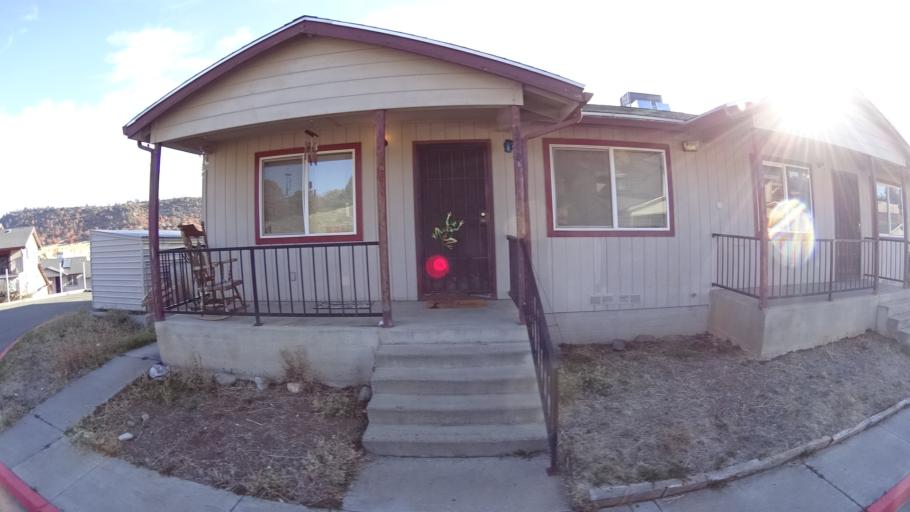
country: US
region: California
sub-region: Siskiyou County
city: Yreka
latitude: 41.7129
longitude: -122.6260
